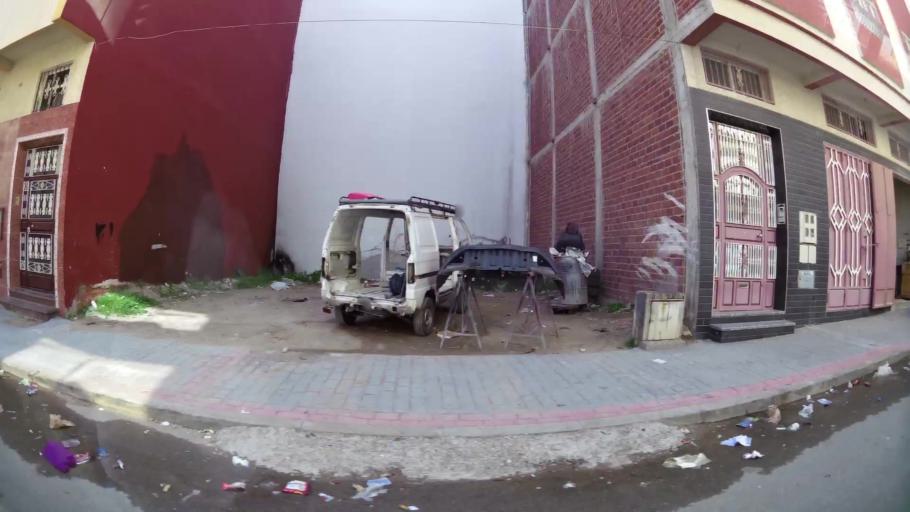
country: MA
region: Tanger-Tetouan
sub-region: Tanger-Assilah
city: Tangier
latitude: 35.7321
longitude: -5.8033
